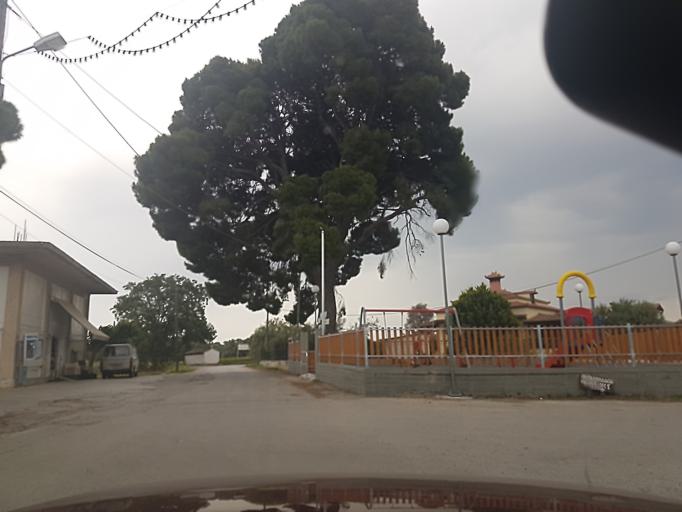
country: GR
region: Central Greece
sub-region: Nomos Evvoias
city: Mytikas
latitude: 38.4508
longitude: 23.6503
